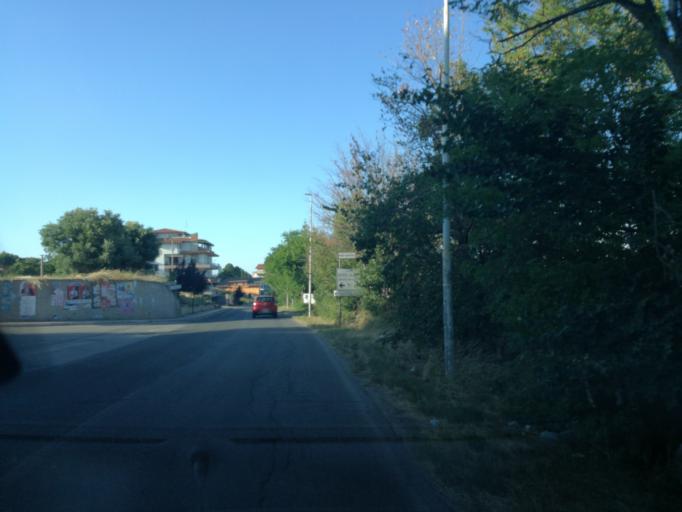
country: IT
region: Molise
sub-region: Provincia di Campobasso
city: Guglionesi
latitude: 41.9198
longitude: 14.9159
